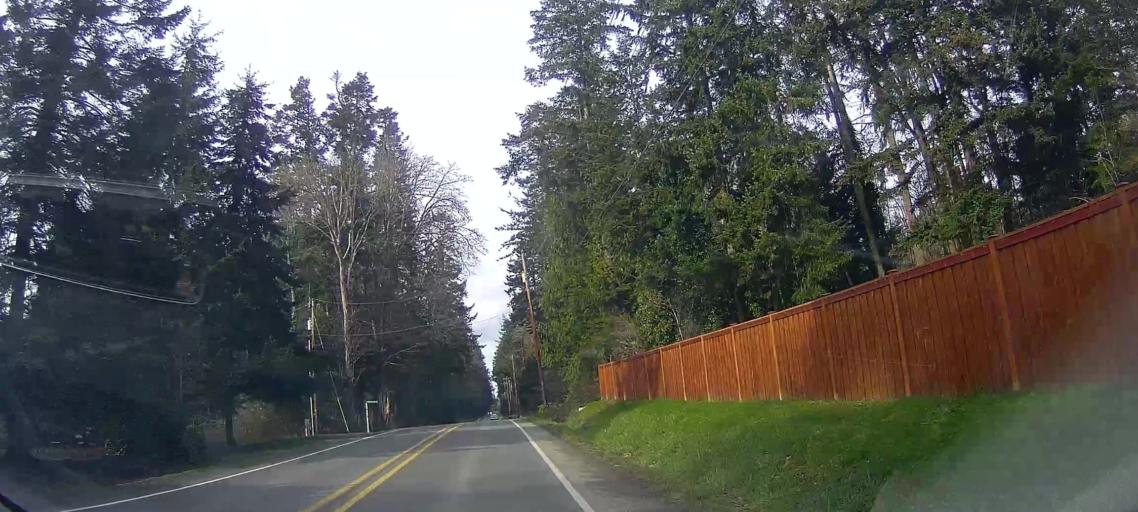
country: US
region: Washington
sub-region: Island County
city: Camano
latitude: 48.1228
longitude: -122.4533
